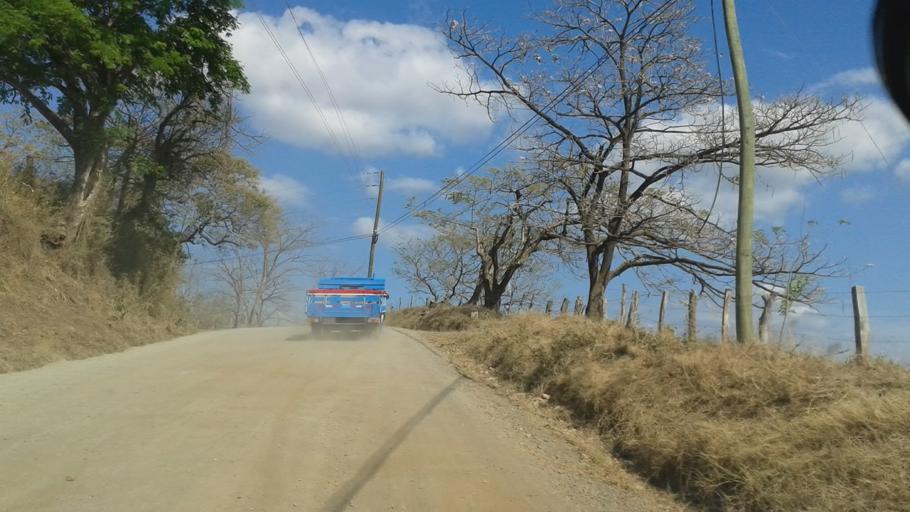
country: CR
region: Guanacaste
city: Santa Cruz
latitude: 10.1138
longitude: -85.7793
